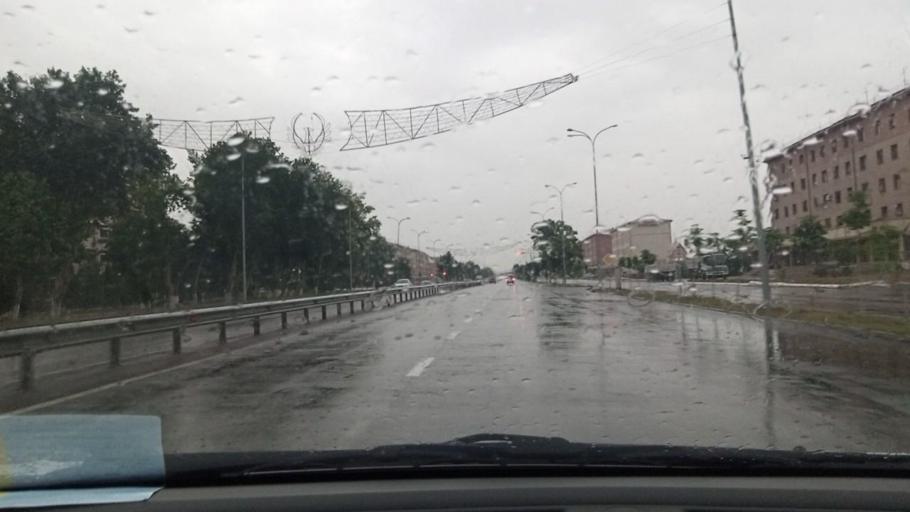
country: UZ
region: Toshkent
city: Ohangaron
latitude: 40.9095
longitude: 69.6232
